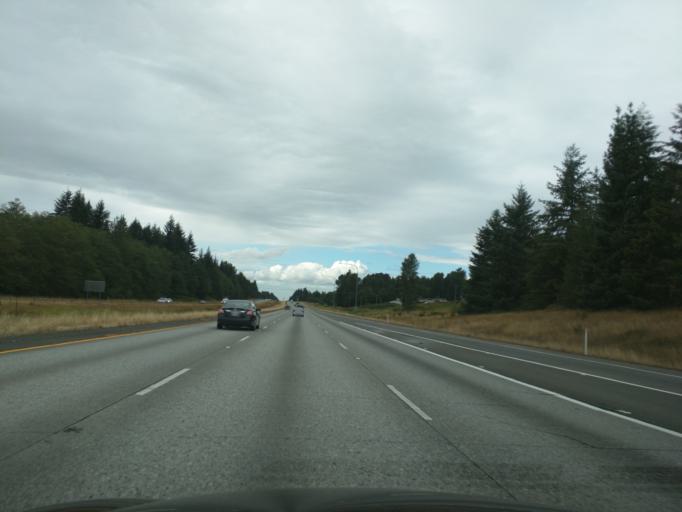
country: US
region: Washington
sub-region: Snohomish County
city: Stanwood
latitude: 48.2699
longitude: -122.2712
